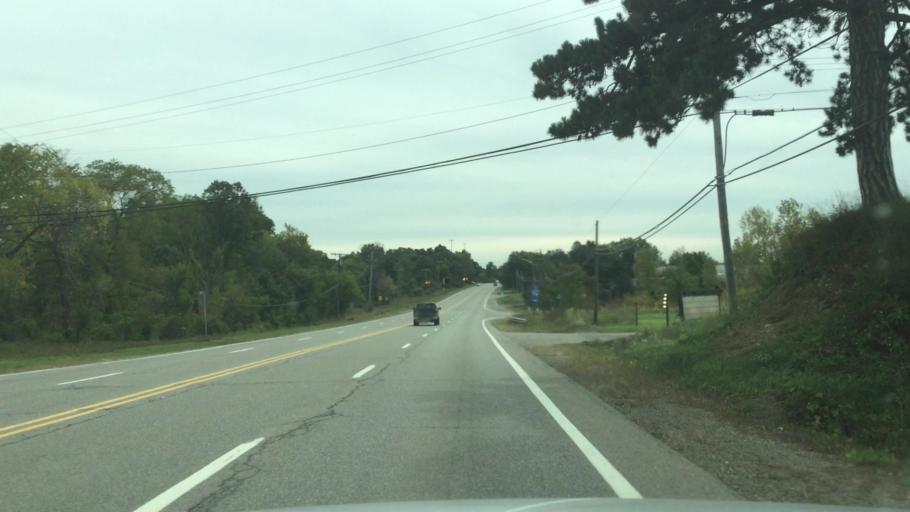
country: US
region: Michigan
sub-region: Oakland County
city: Ortonville
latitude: 42.7816
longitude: -83.5004
